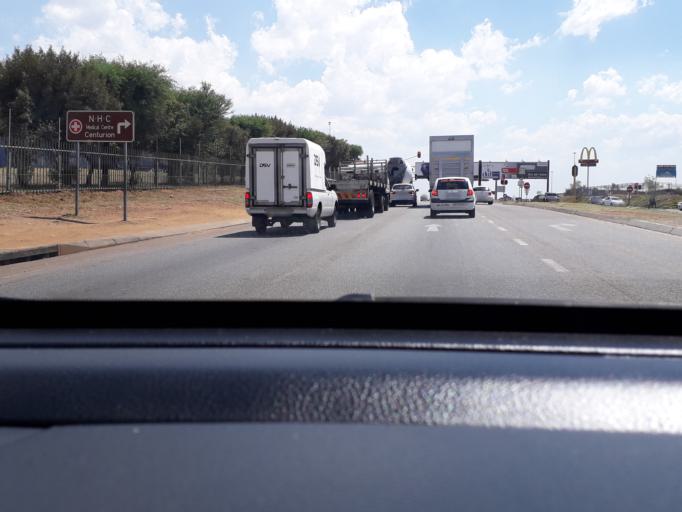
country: ZA
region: Gauteng
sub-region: City of Tshwane Metropolitan Municipality
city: Centurion
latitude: -25.9104
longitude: 28.1631
